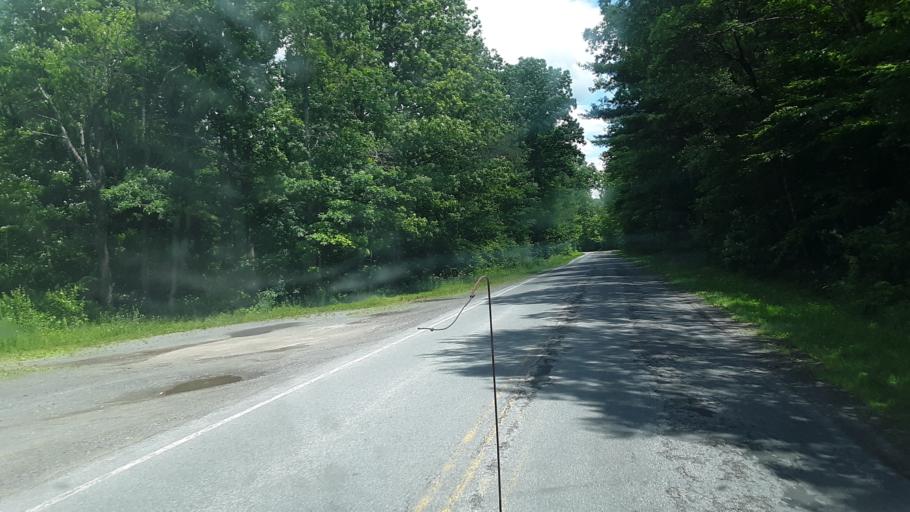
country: US
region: New York
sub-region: Oneida County
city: Rome
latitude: 43.2633
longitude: -75.5811
